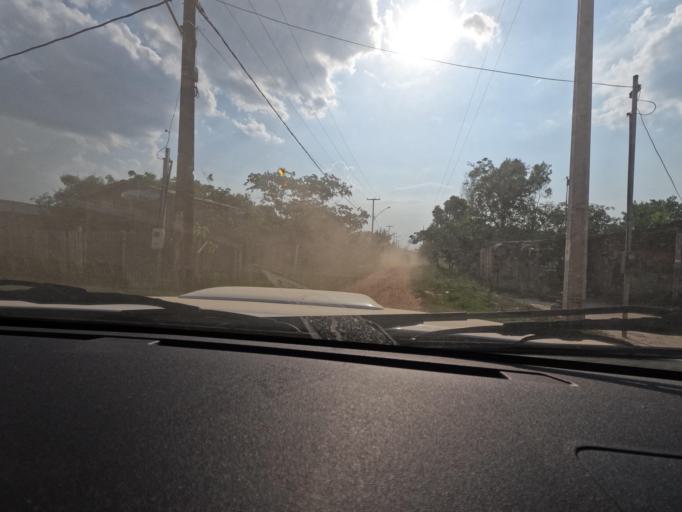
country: BR
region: Rondonia
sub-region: Porto Velho
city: Porto Velho
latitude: -8.5752
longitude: -63.9949
